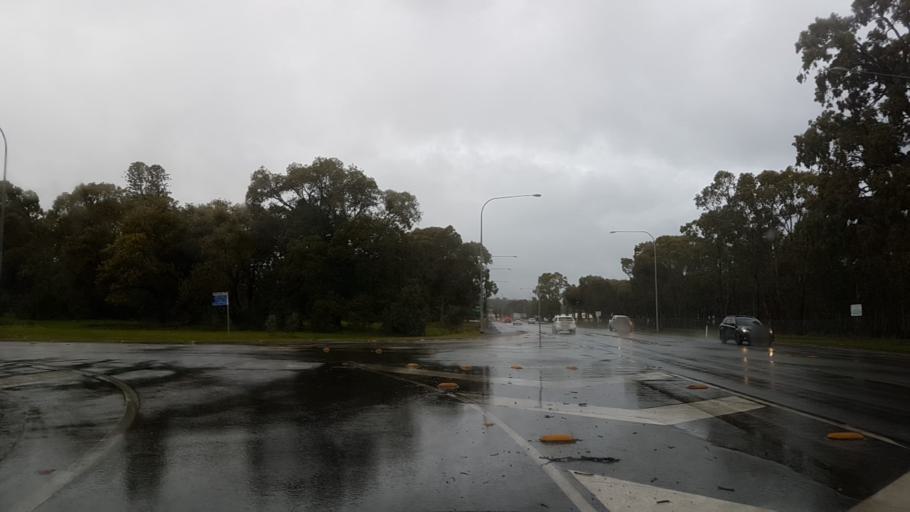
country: AU
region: South Australia
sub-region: Marion
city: Trott Park
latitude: -35.0810
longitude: 138.5820
